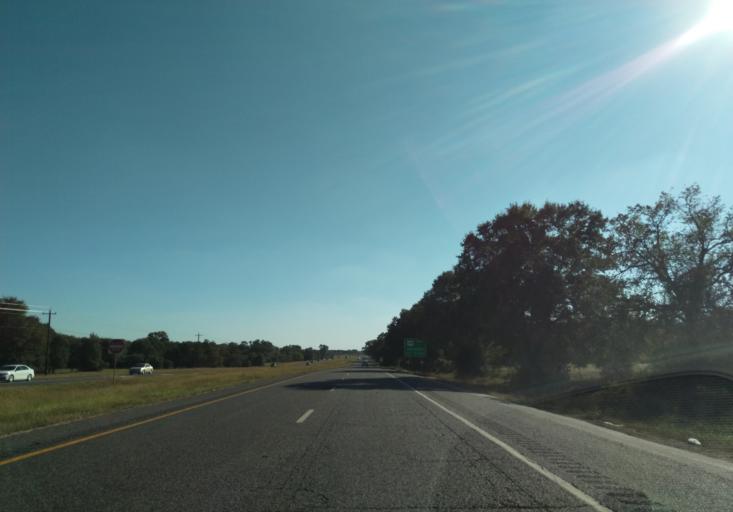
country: US
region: Texas
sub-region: Waller County
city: Hempstead
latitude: 30.1277
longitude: -96.0739
